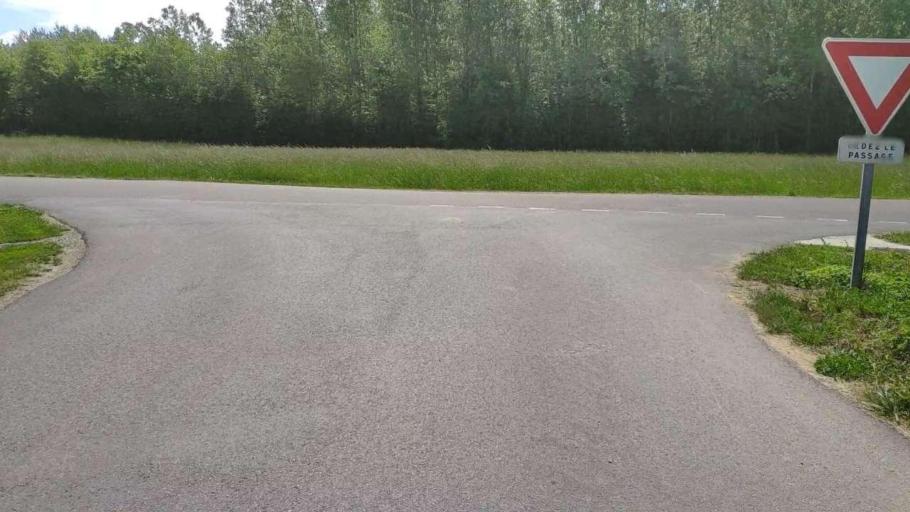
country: FR
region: Franche-Comte
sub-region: Departement du Jura
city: Bletterans
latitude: 46.7063
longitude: 5.4254
